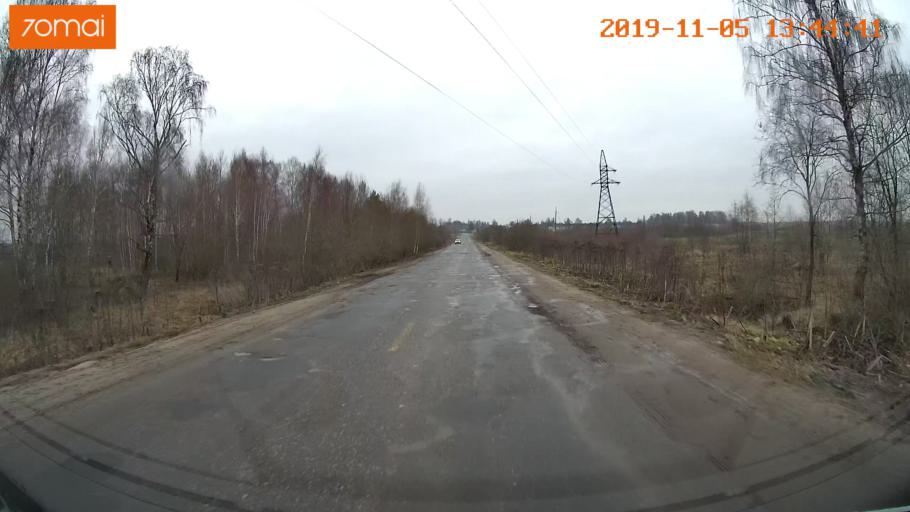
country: RU
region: Ivanovo
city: Shuya
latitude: 56.9827
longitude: 41.4112
